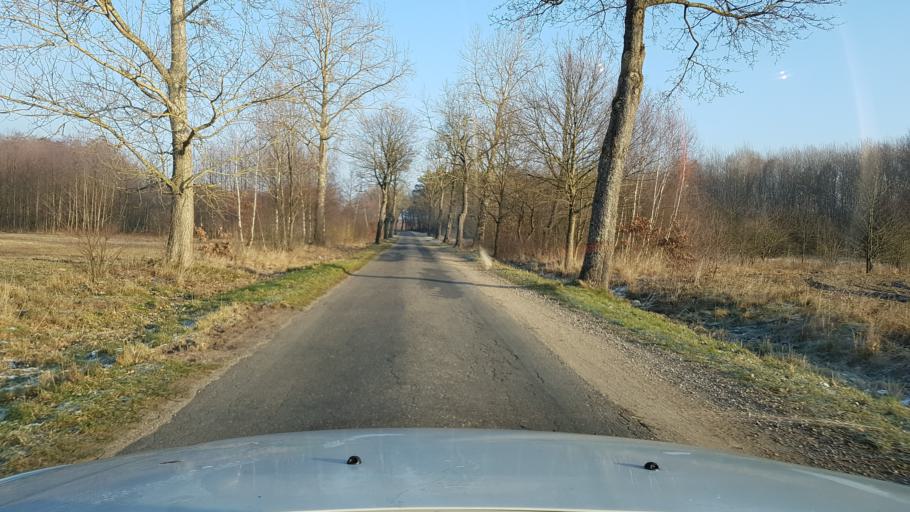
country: PL
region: West Pomeranian Voivodeship
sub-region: Powiat bialogardzki
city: Bialogard
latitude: 54.0583
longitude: 16.0787
